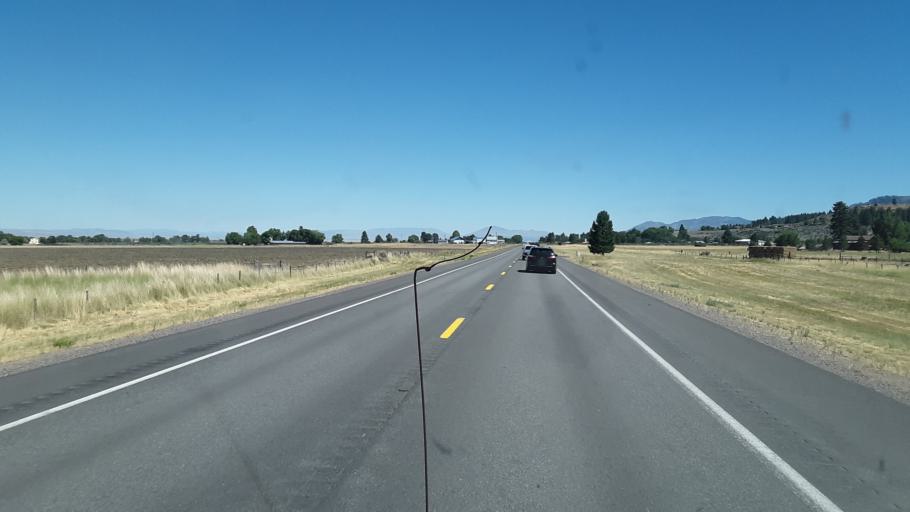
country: US
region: California
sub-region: Lassen County
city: Janesville
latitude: 40.2994
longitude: -120.5165
